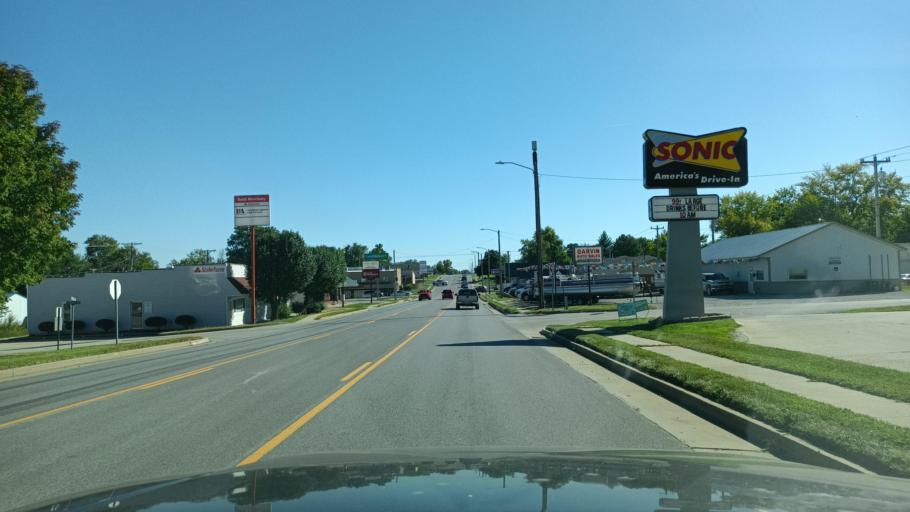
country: US
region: Missouri
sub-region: Macon County
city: Macon
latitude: 39.7439
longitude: -92.4652
